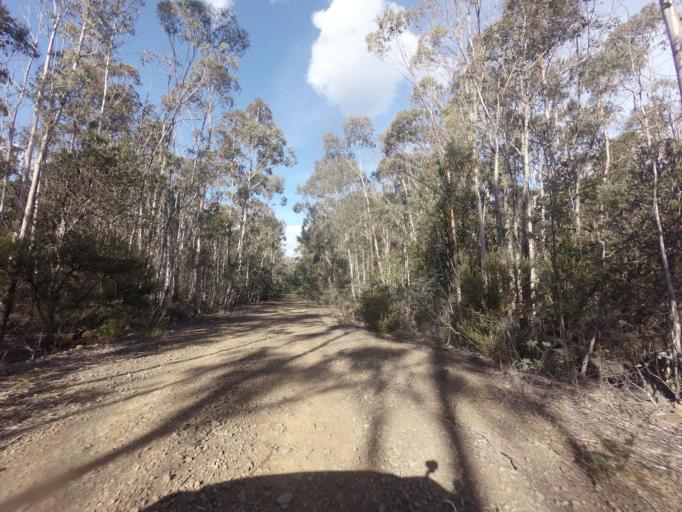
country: AU
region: Tasmania
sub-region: Break O'Day
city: St Helens
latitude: -41.8477
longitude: 148.0544
